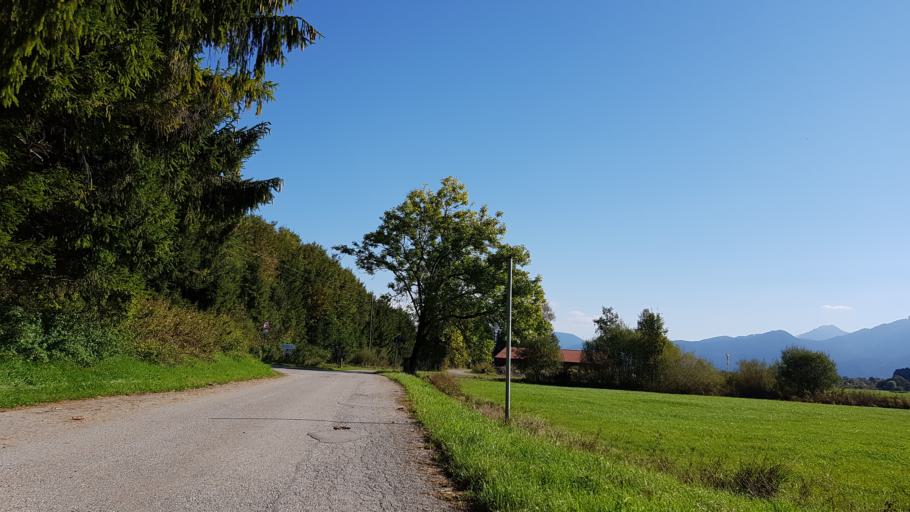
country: DE
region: Bavaria
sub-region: Swabia
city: Fuessen
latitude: 47.5830
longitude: 10.6829
